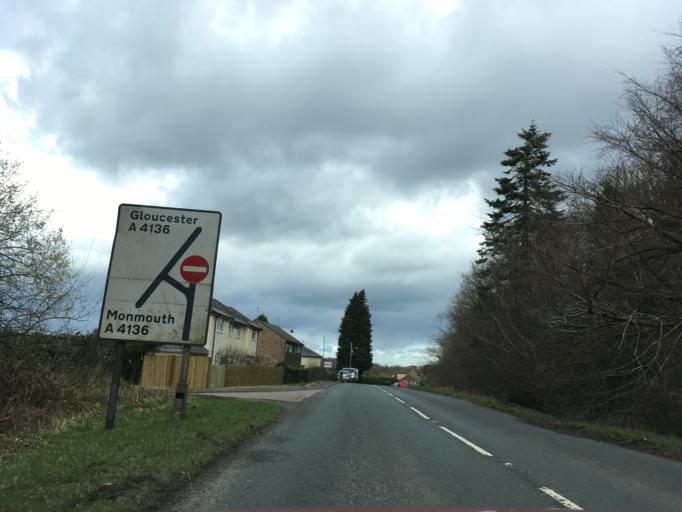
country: GB
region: England
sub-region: Gloucestershire
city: Lydbrook
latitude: 51.8141
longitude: -2.5928
